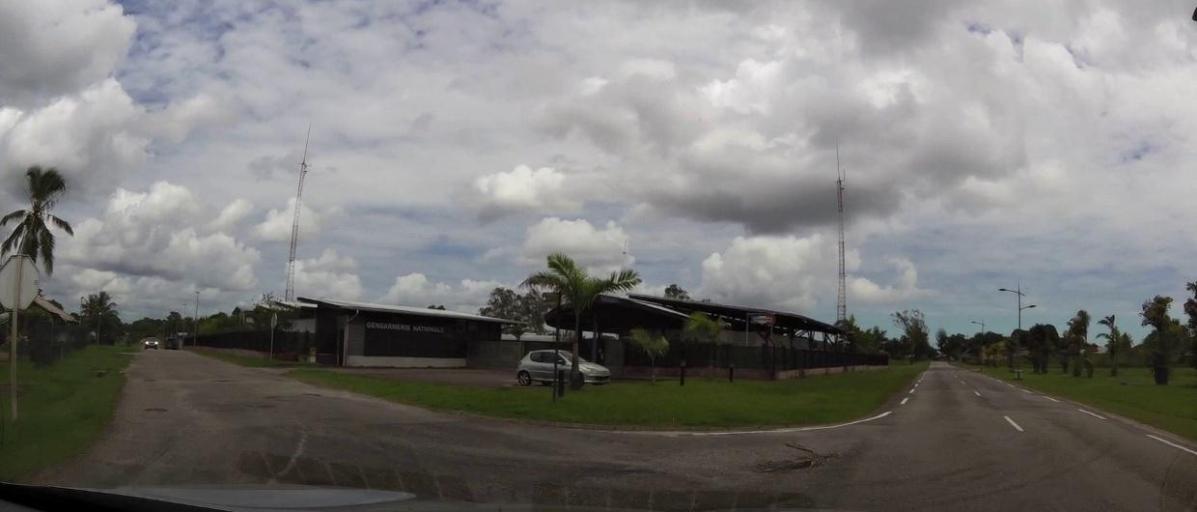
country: GF
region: Guyane
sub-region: Guyane
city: Sinnamary
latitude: 5.3737
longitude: -52.9515
